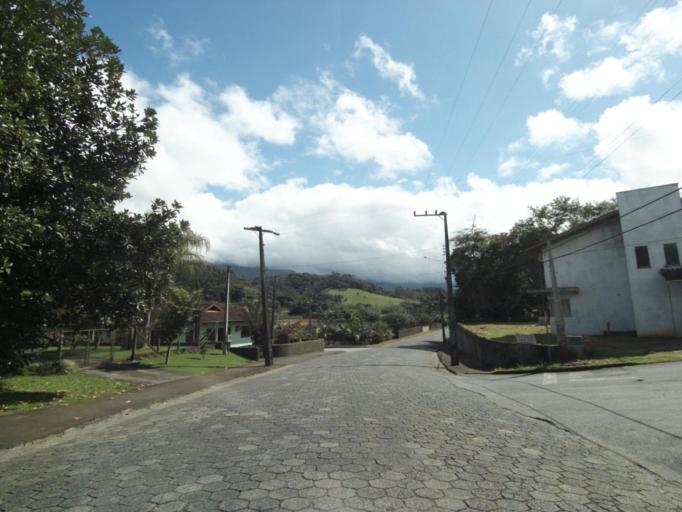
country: BR
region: Santa Catarina
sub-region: Pomerode
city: Pomerode
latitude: -26.7004
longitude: -49.1728
